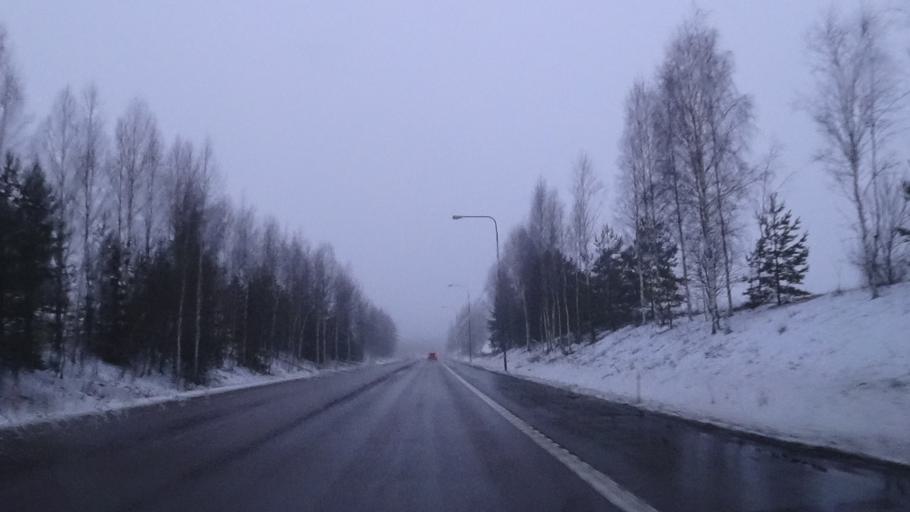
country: FI
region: Paijanne Tavastia
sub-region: Lahti
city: Hollola
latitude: 60.9824
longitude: 25.4607
